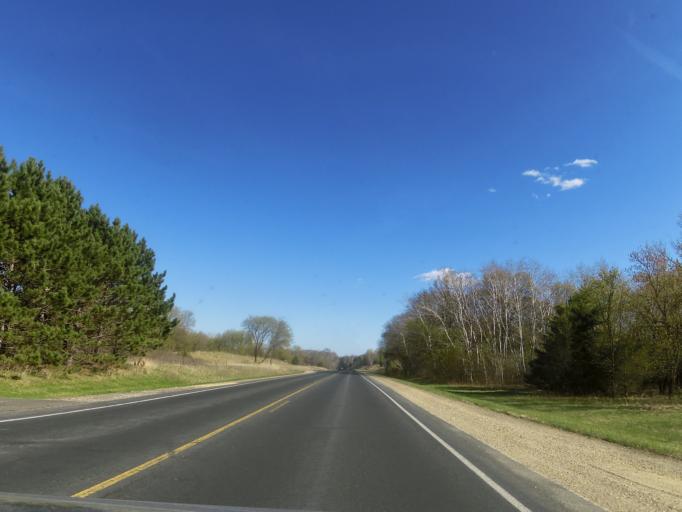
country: US
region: Minnesota
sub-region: Washington County
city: Bayport
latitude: 45.0546
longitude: -92.7252
